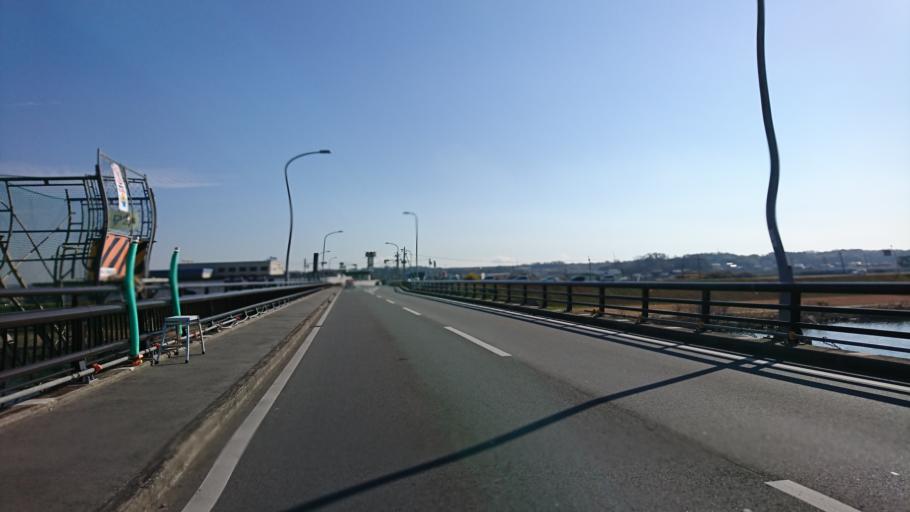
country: JP
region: Hyogo
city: Ono
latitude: 34.7968
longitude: 134.9001
